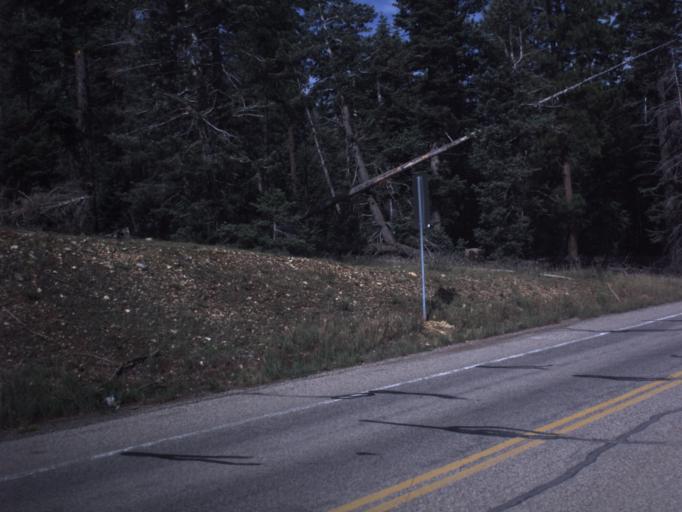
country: US
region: Utah
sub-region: Iron County
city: Parowan
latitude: 37.5186
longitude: -112.6480
